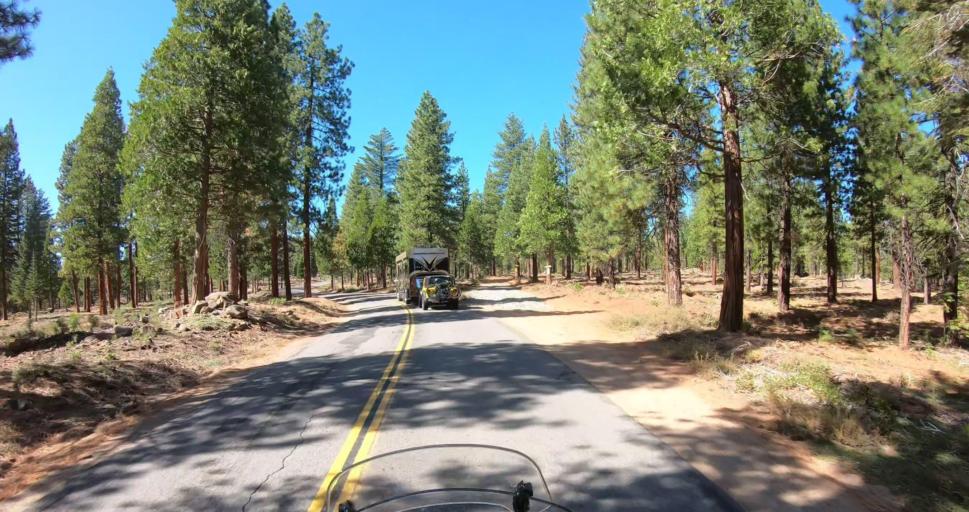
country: US
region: California
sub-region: Lassen County
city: Susanville
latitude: 40.4432
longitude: -120.7499
